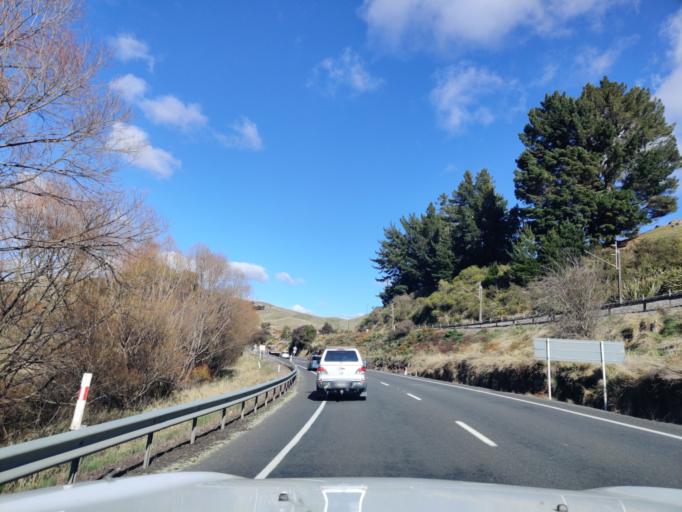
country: NZ
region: Manawatu-Wanganui
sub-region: Ruapehu District
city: Waiouru
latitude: -39.5646
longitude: 175.6975
